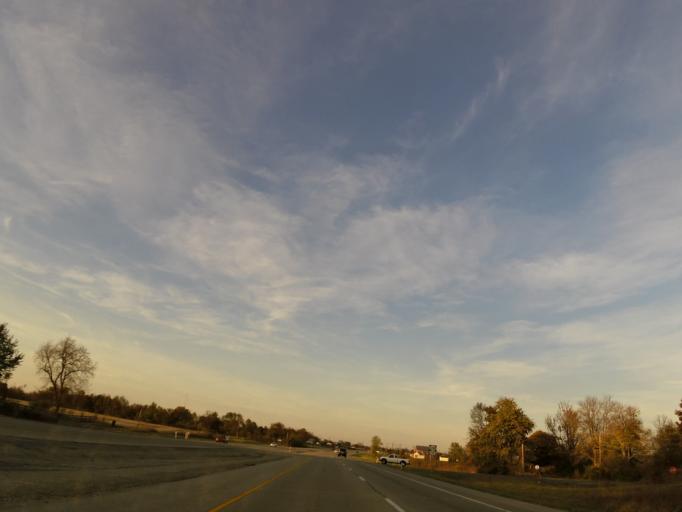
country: US
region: Kentucky
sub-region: Jessamine County
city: Nicholasville
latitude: 37.8148
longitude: -84.5983
